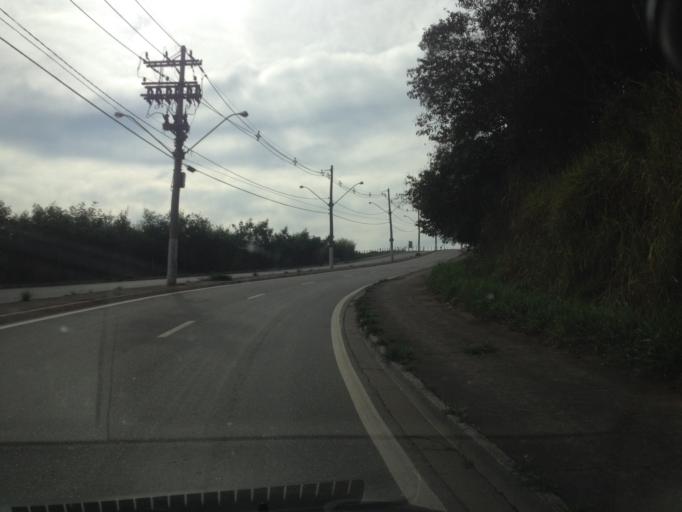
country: BR
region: Sao Paulo
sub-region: Itu
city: Itu
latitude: -23.2705
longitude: -47.3252
